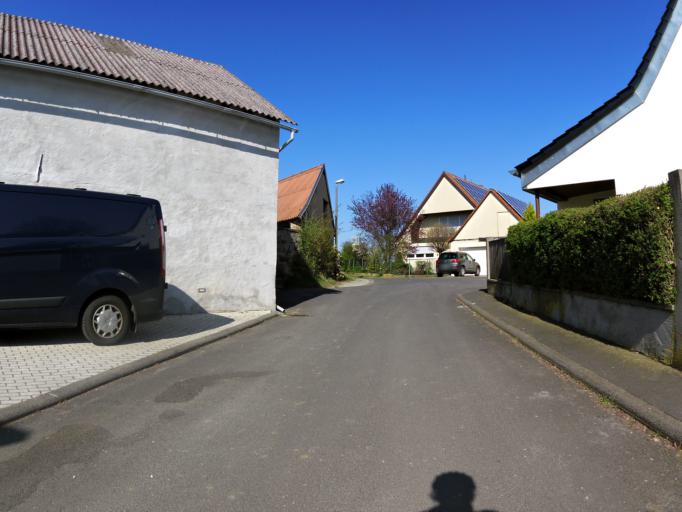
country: DE
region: Bavaria
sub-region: Regierungsbezirk Unterfranken
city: Prosselsheim
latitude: 49.8239
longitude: 10.1080
